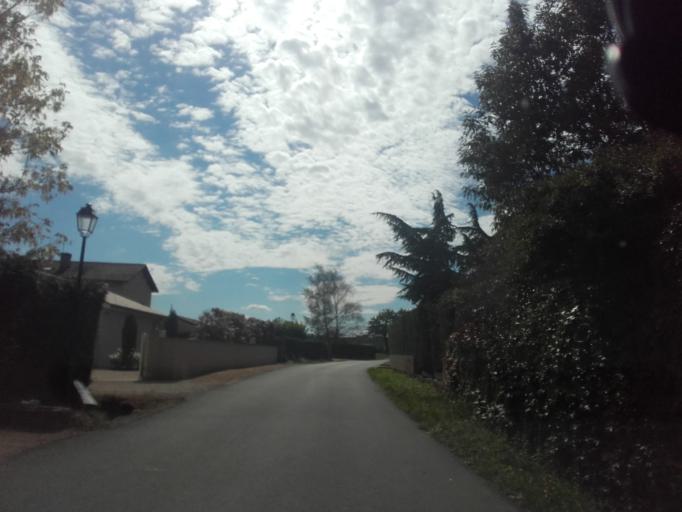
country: FR
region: Bourgogne
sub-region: Departement de Saone-et-Loire
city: Creches-sur-Saone
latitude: 46.2532
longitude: 4.7672
